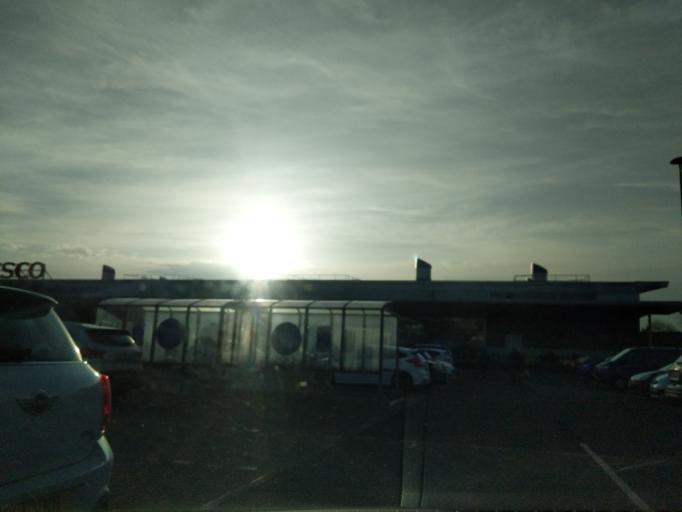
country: GB
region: Scotland
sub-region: South Lanarkshire
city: Carluke
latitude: 55.7291
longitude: -3.8370
